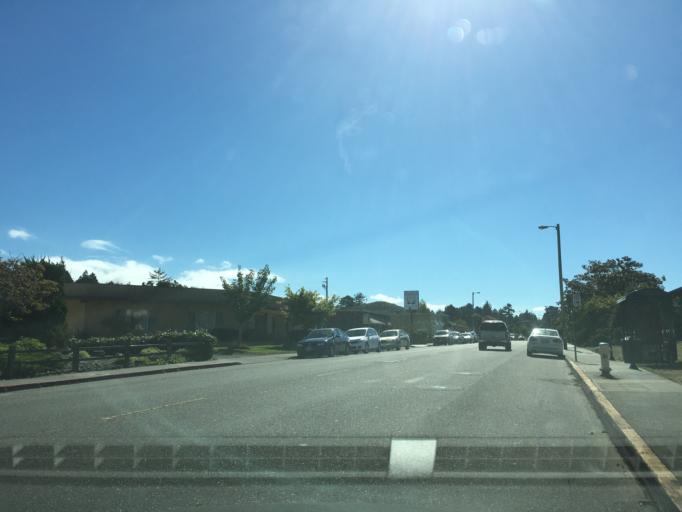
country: US
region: California
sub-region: Humboldt County
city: Myrtletown
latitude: 40.7880
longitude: -124.1397
